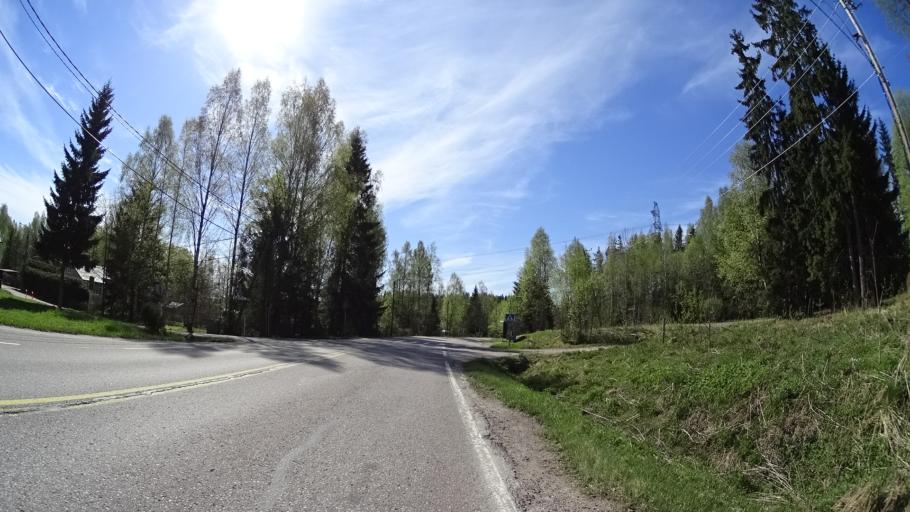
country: FI
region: Uusimaa
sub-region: Helsinki
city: Nurmijaervi
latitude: 60.3856
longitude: 24.8371
